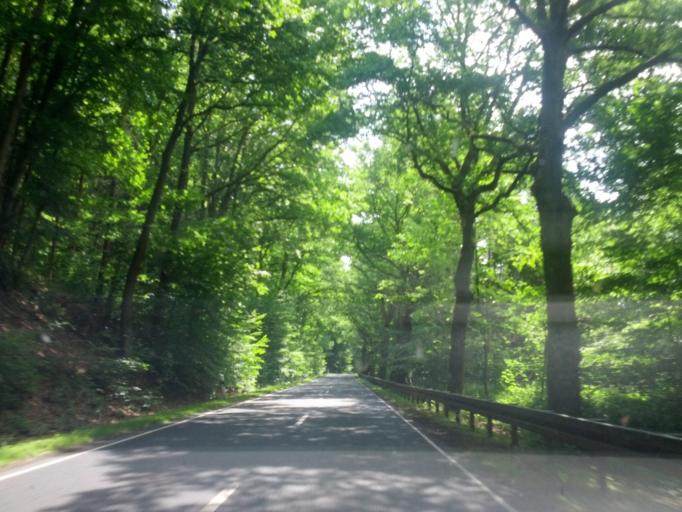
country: DE
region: Thuringia
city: Stadtlengsfeld
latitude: 50.7970
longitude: 10.1010
